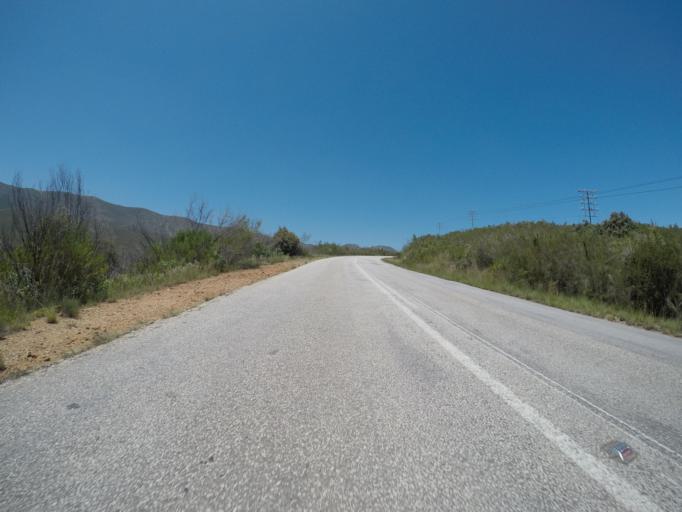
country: ZA
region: Eastern Cape
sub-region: Cacadu District Municipality
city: Kareedouw
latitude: -33.8860
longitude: 24.0797
